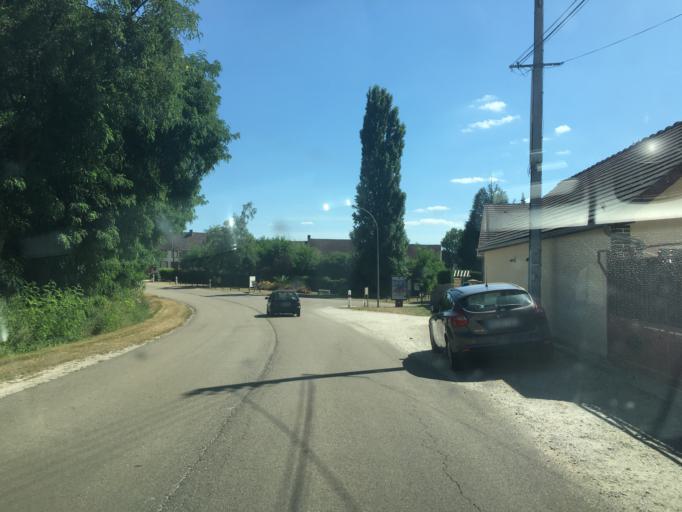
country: FR
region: Bourgogne
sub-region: Departement de l'Yonne
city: Fleury-la-Vallee
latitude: 47.8600
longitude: 3.4464
